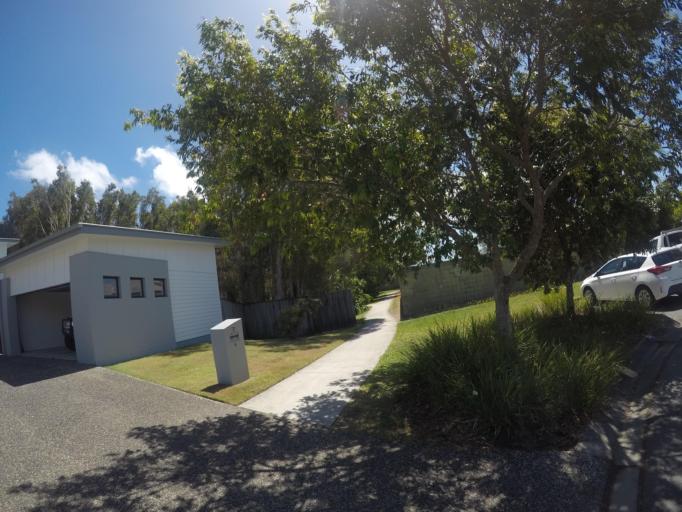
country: AU
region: Queensland
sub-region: Sunshine Coast
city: Mooloolaba
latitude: -26.6143
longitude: 153.0929
